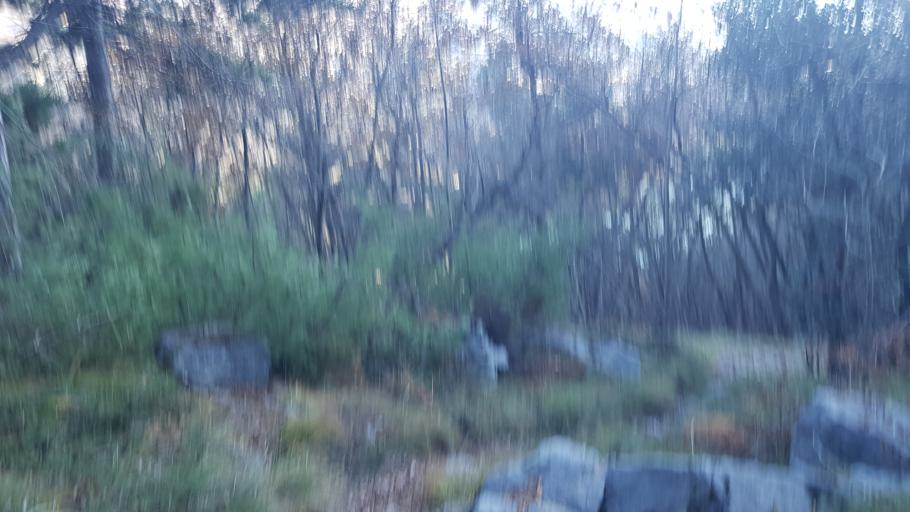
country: IT
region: Trentino-Alto Adige
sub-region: Provincia di Trento
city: Padergnone
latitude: 46.0755
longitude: 10.9795
